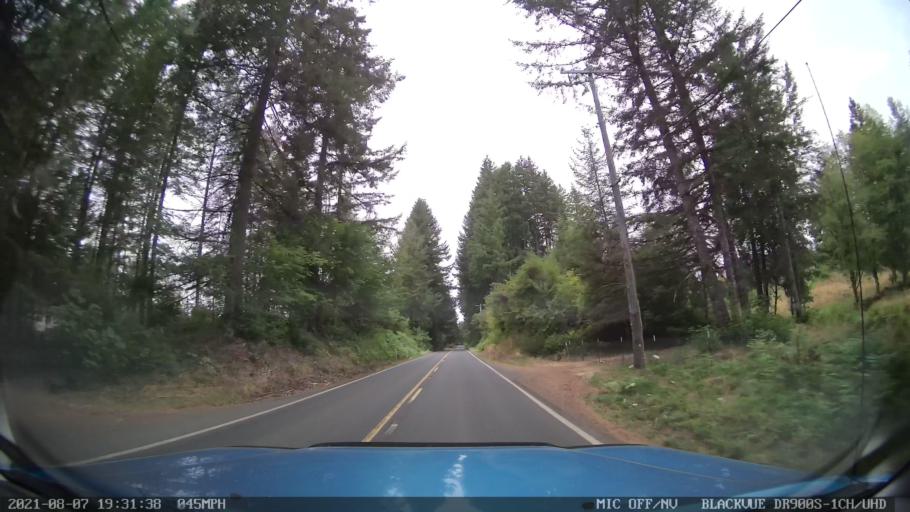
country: US
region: Oregon
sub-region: Linn County
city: Lyons
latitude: 44.8931
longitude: -122.6358
